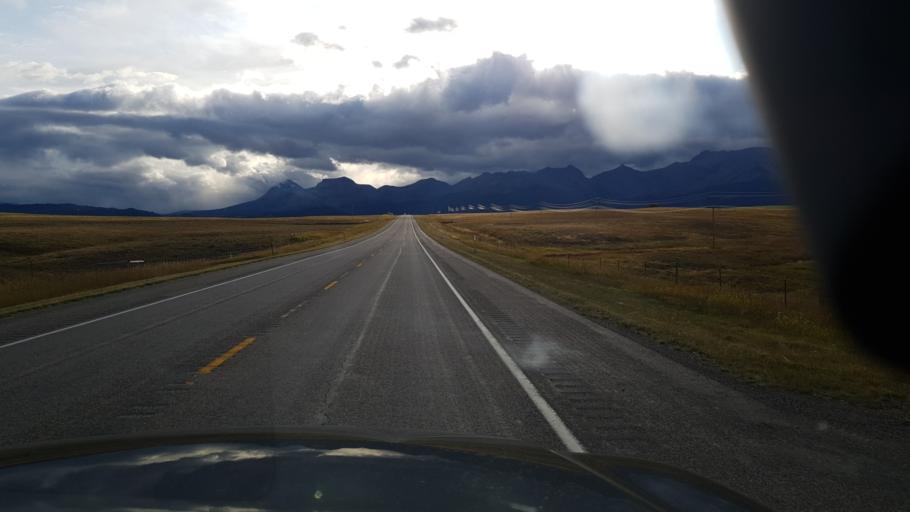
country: US
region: Montana
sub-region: Glacier County
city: South Browning
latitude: 48.4663
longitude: -113.1569
